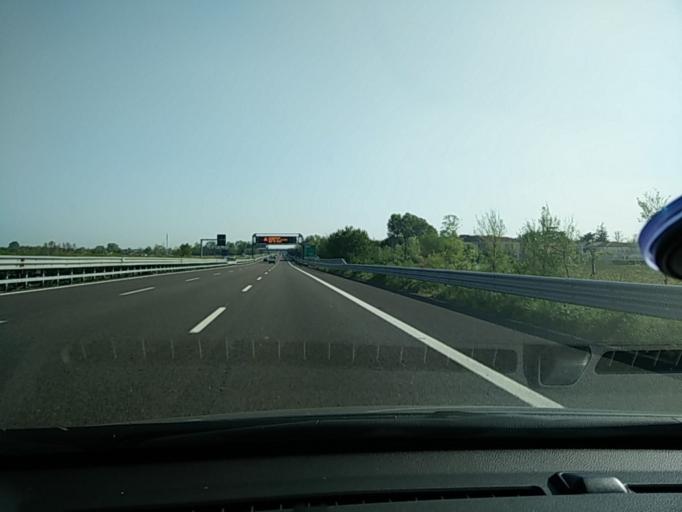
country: IT
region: Veneto
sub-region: Provincia di Venezia
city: Marcon-Gaggio-Colmello
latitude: 45.5582
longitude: 12.2735
